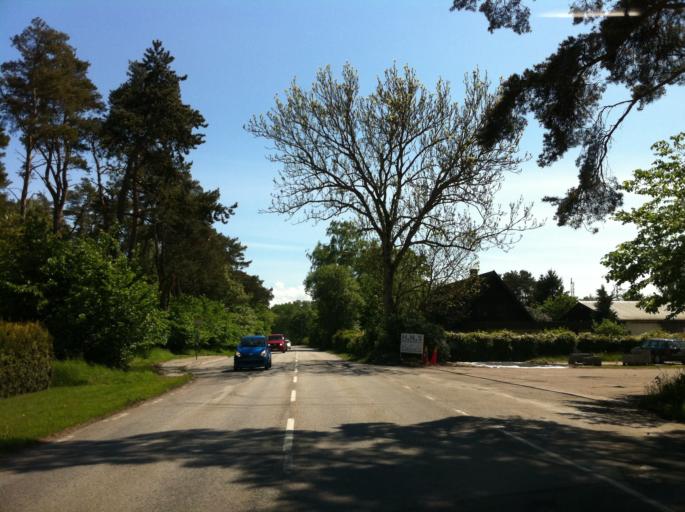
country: SE
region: Skane
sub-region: Kavlinge Kommun
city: Hofterup
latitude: 55.8063
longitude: 12.9827
